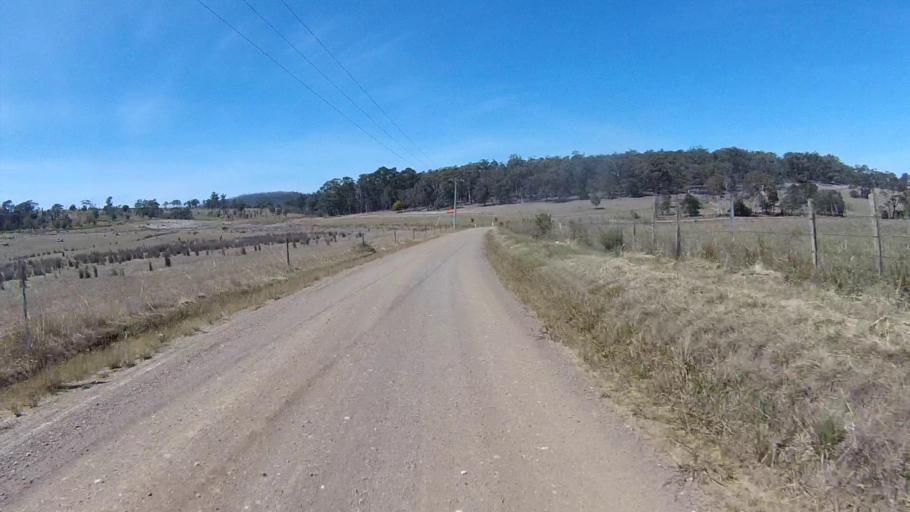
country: AU
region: Tasmania
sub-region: Sorell
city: Sorell
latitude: -42.7770
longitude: 147.6542
